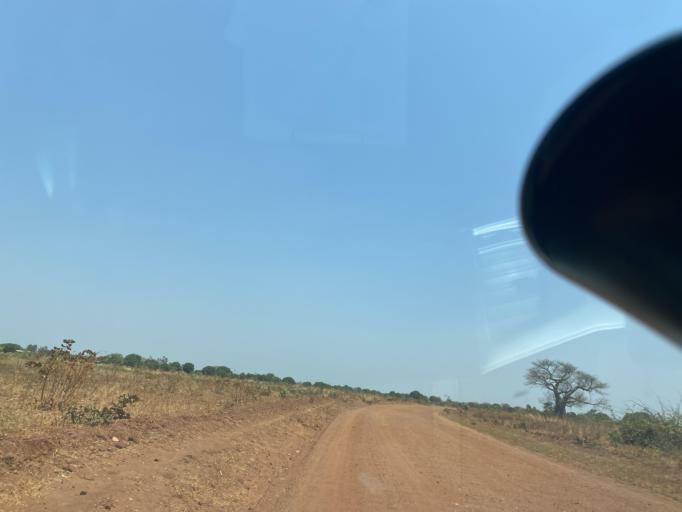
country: ZM
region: Southern
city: Nakambala
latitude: -15.5035
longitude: 27.9196
